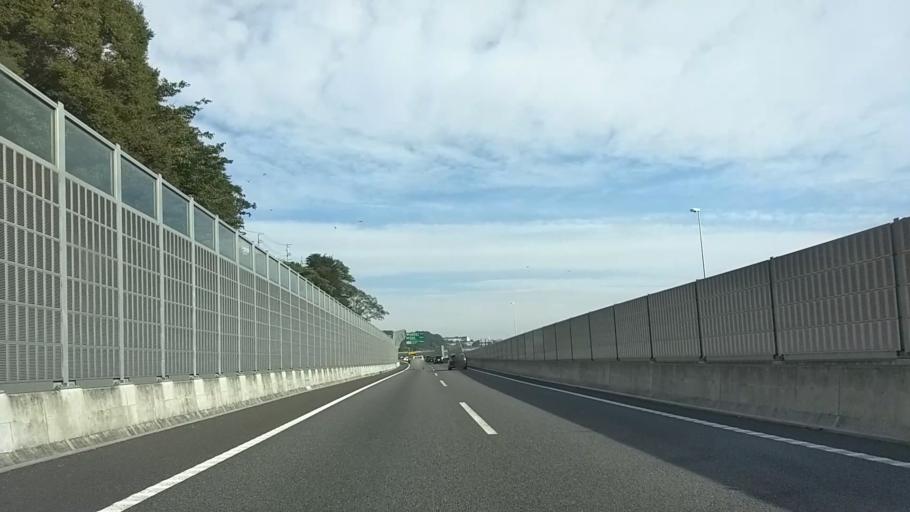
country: JP
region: Kanagawa
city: Zama
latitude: 35.4931
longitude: 139.3680
